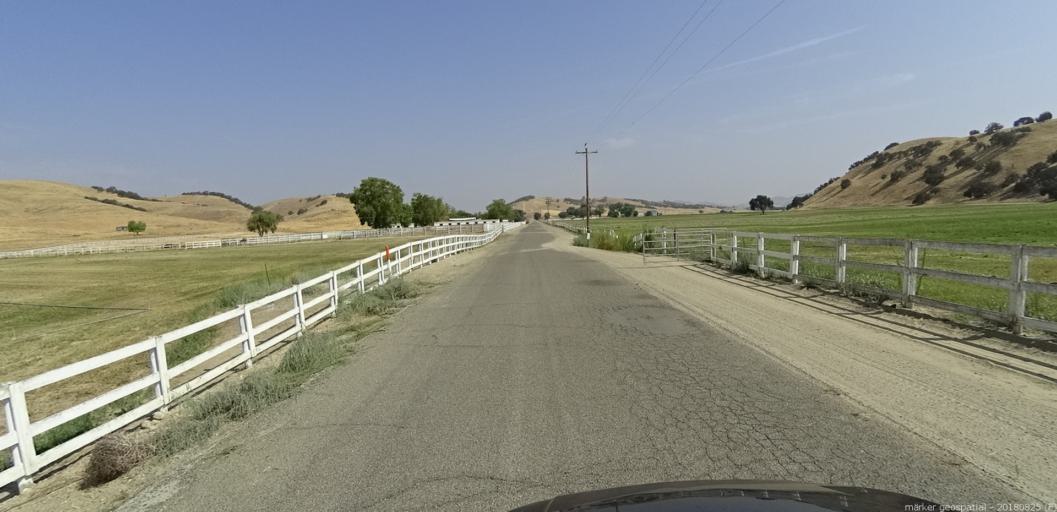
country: US
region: California
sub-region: San Luis Obispo County
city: San Miguel
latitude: 35.8276
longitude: -120.6562
